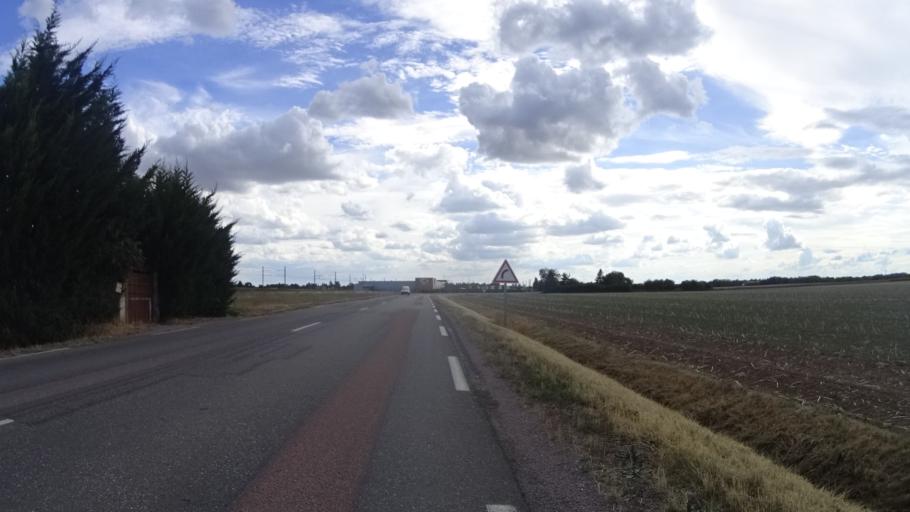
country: FR
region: Bourgogne
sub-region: Departement de la Cote-d'Or
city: Seurre
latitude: 47.0129
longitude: 5.1596
